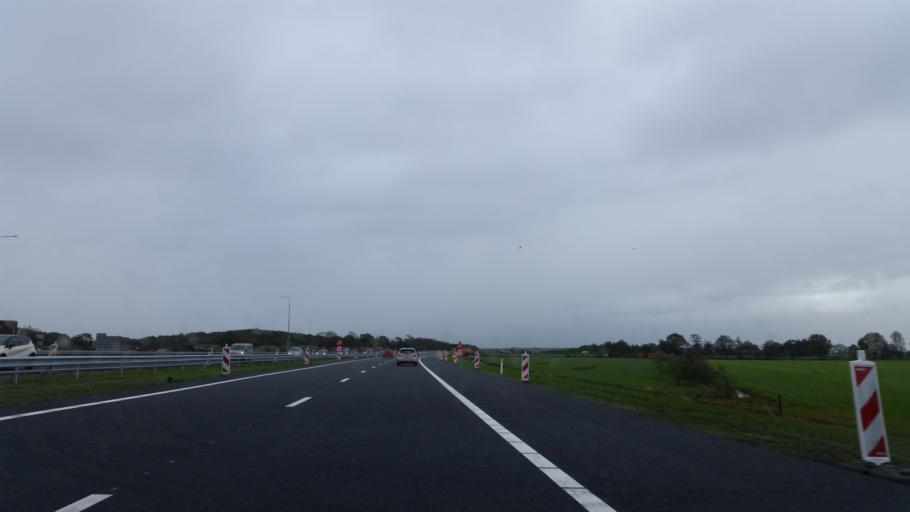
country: NL
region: Friesland
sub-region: Gemeente Skarsterlan
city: Joure
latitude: 52.9552
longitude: 5.7829
